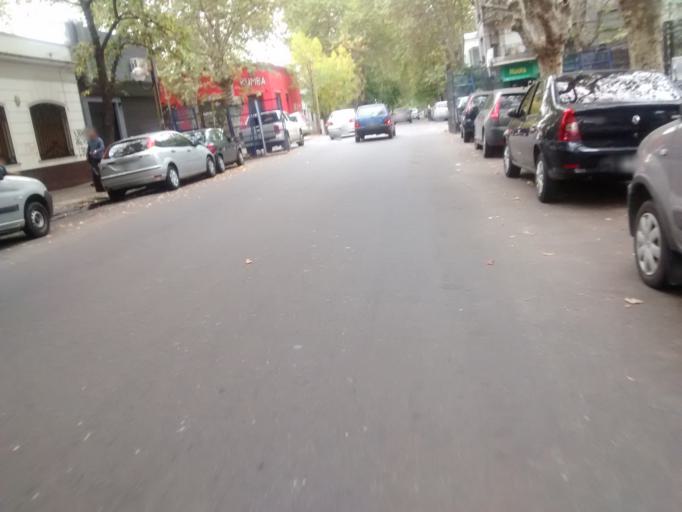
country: AR
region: Buenos Aires
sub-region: Partido de La Plata
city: La Plata
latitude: -34.9248
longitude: -57.9517
